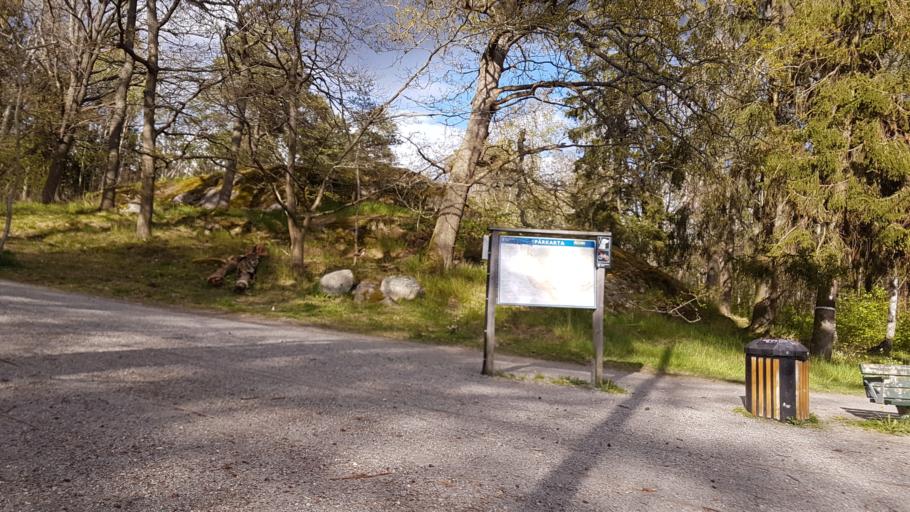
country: SE
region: Stockholm
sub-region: Nacka Kommun
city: Nacka
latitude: 59.2966
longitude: 18.1170
